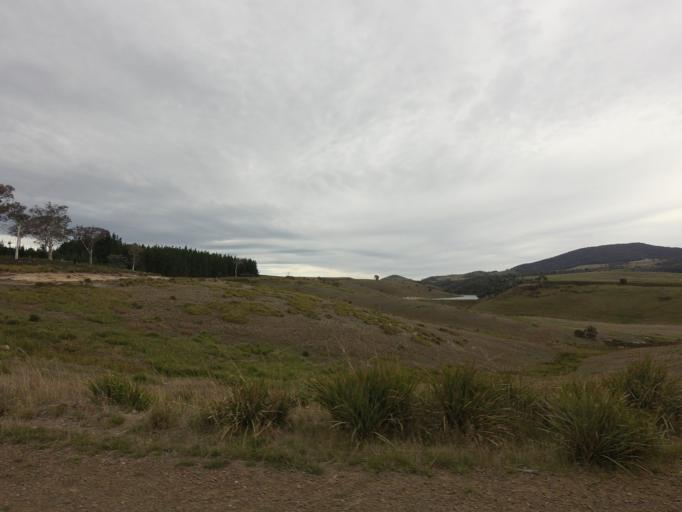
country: AU
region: Tasmania
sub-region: Derwent Valley
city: New Norfolk
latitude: -42.3969
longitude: 146.9132
